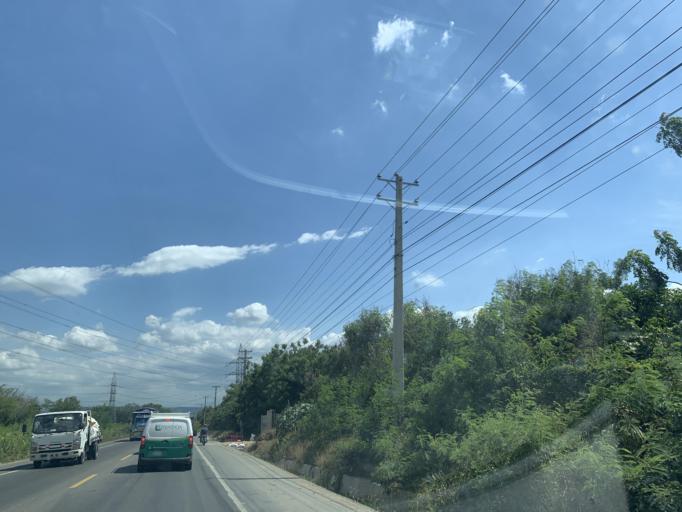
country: DO
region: Santiago
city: Villa Bisono
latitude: 19.5622
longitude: -70.8583
